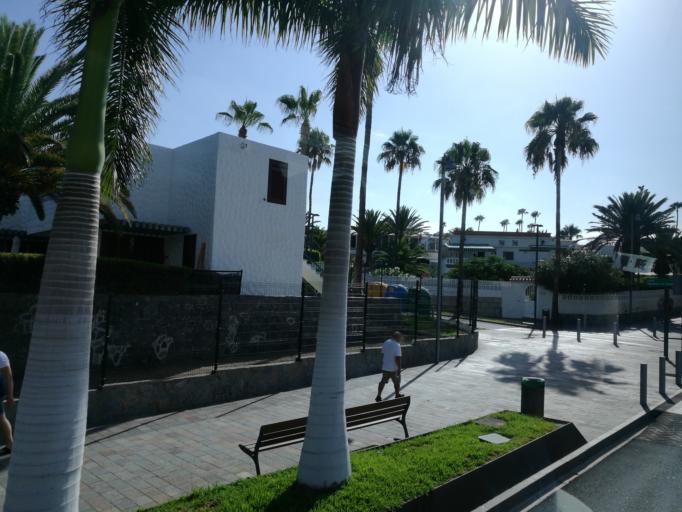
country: ES
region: Canary Islands
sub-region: Provincia de Santa Cruz de Tenerife
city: Playa de las Americas
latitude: 28.0687
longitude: -16.7310
